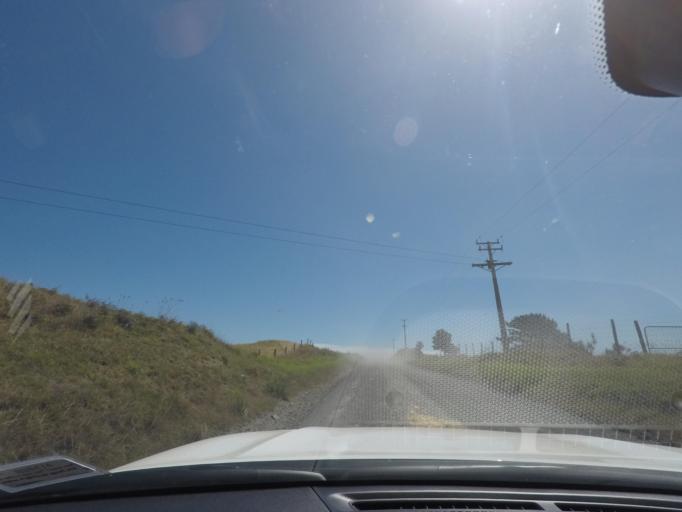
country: NZ
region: Auckland
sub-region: Auckland
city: Parakai
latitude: -36.5845
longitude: 174.2942
